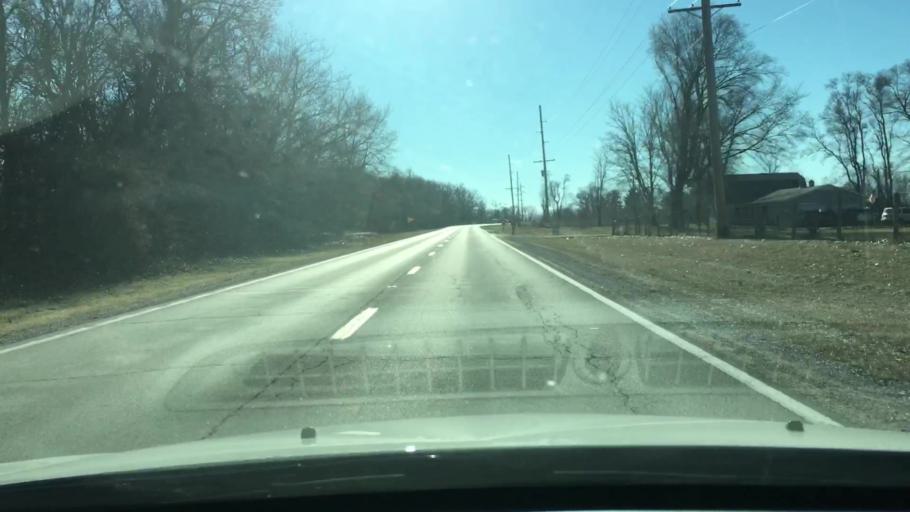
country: US
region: Illinois
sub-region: Cass County
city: Beardstown
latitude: 39.9461
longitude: -90.4864
